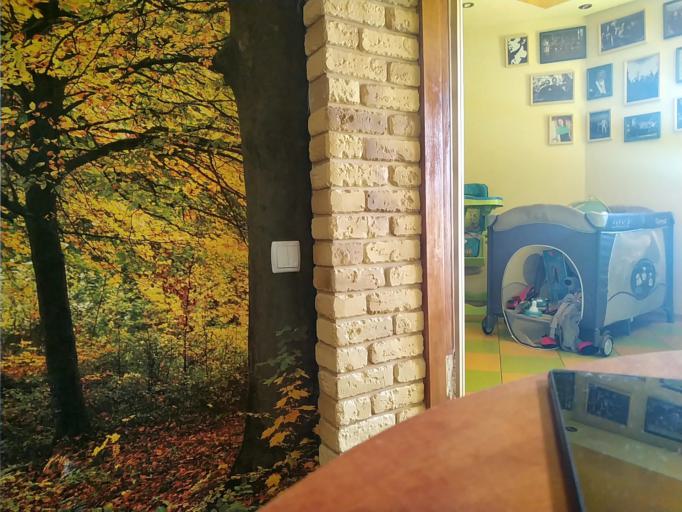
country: RU
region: Tverskaya
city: Vyshniy Volochek
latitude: 57.5406
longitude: 34.5998
